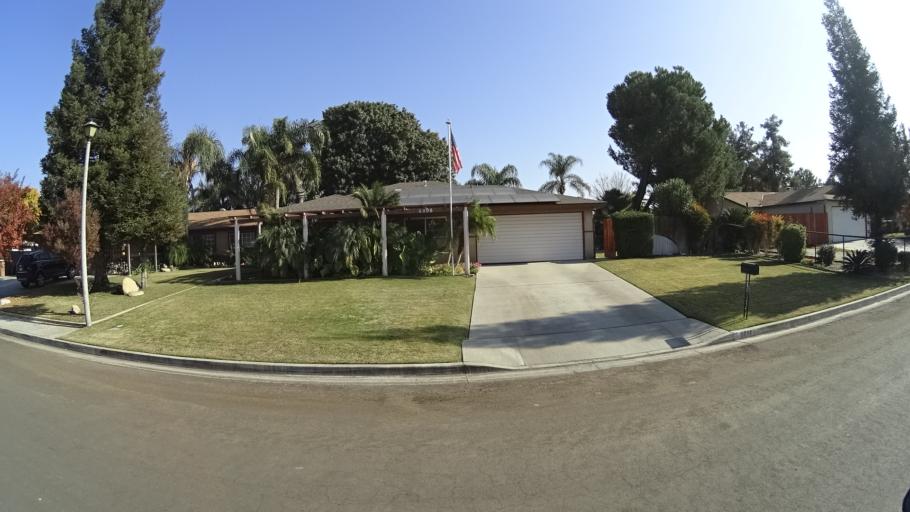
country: US
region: California
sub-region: Kern County
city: Greenfield
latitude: 35.2757
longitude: -119.0154
